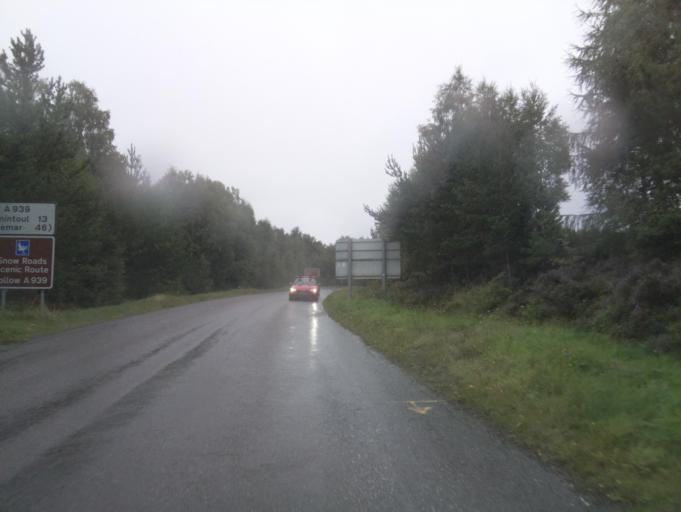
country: GB
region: Scotland
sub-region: Highland
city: Grantown on Spey
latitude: 57.3159
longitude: -3.5899
